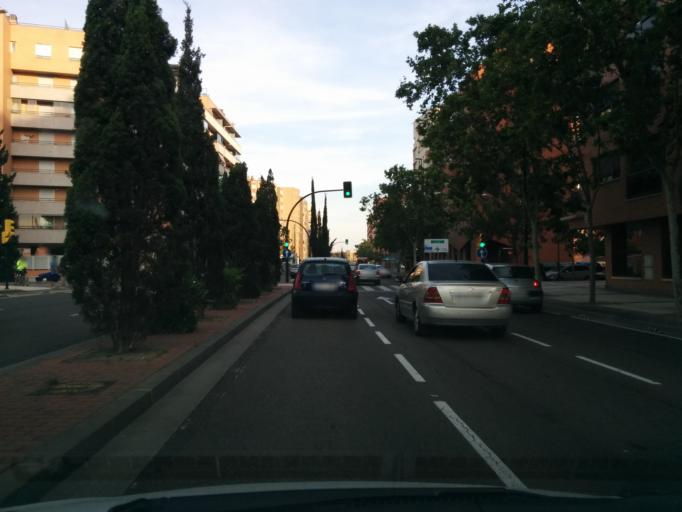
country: ES
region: Aragon
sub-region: Provincia de Zaragoza
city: Zaragoza
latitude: 41.6636
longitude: -0.8662
